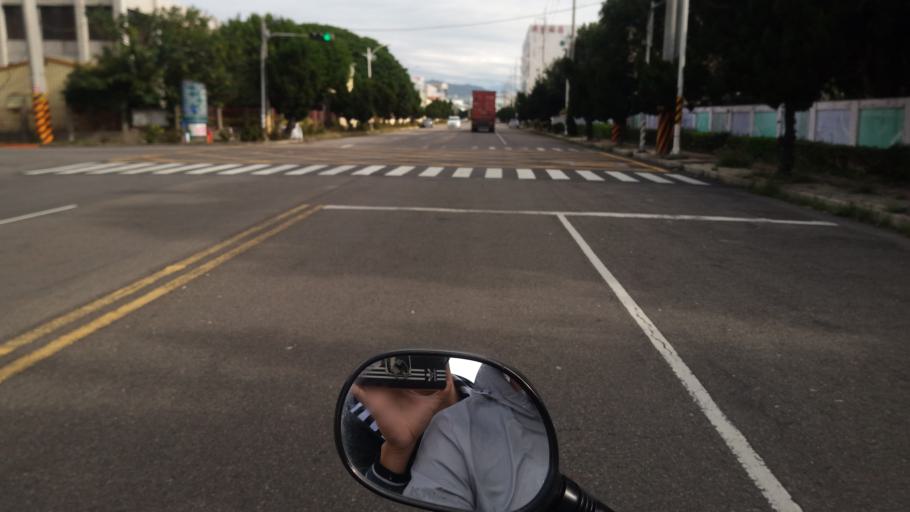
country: TW
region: Taiwan
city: Fengyuan
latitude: 24.4070
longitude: 120.6480
